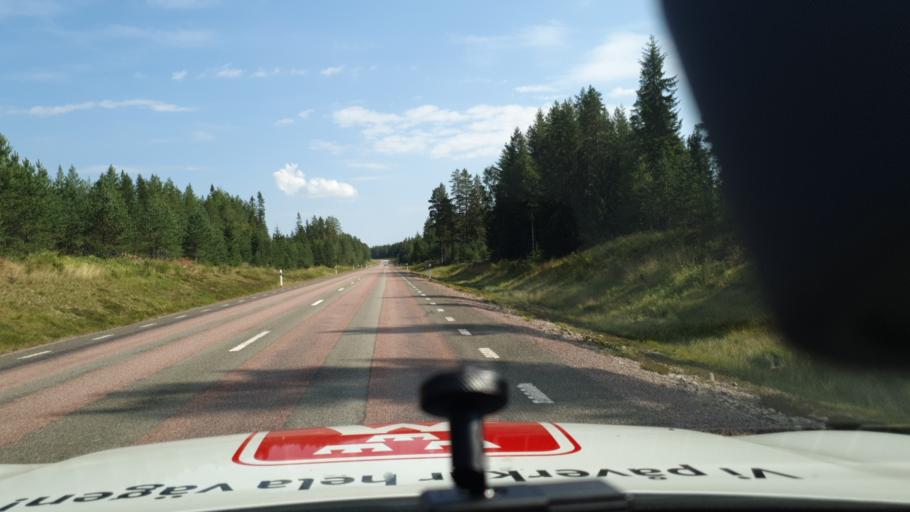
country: SE
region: Dalarna
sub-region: Malung-Saelens kommun
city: Malung
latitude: 60.5639
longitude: 13.5512
